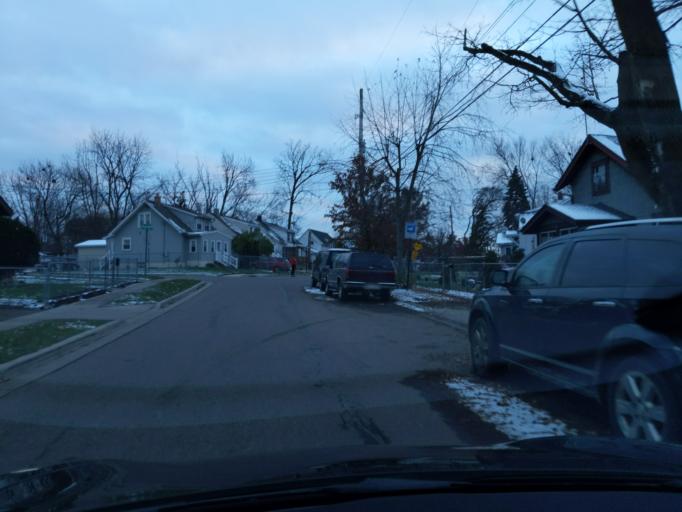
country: US
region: Michigan
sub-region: Ingham County
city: Lansing
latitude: 42.7557
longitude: -84.5373
